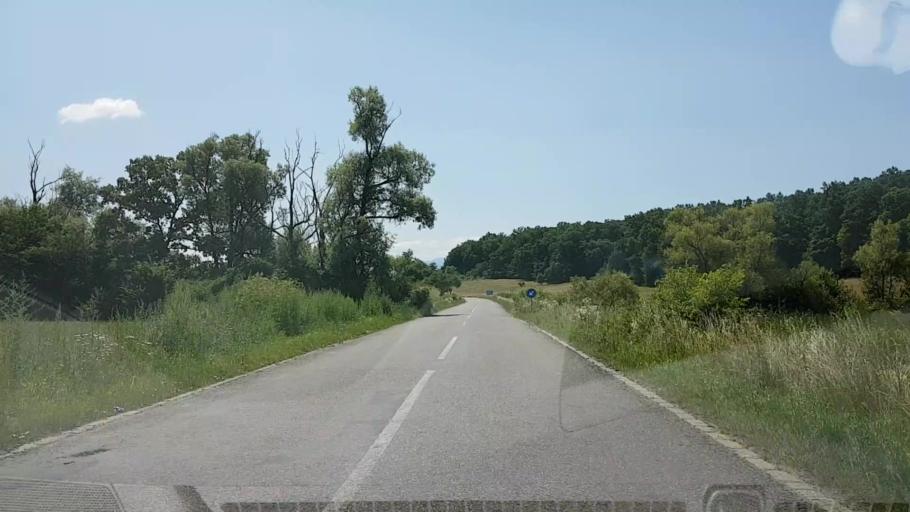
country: RO
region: Brasov
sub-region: Comuna Cincu
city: Cincu
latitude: 45.8729
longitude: 24.8202
